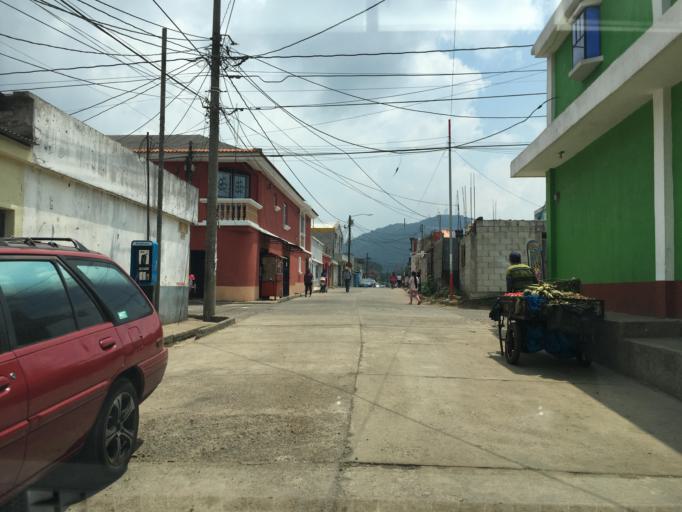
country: GT
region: Guatemala
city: Villa Canales
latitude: 14.4070
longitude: -90.5476
